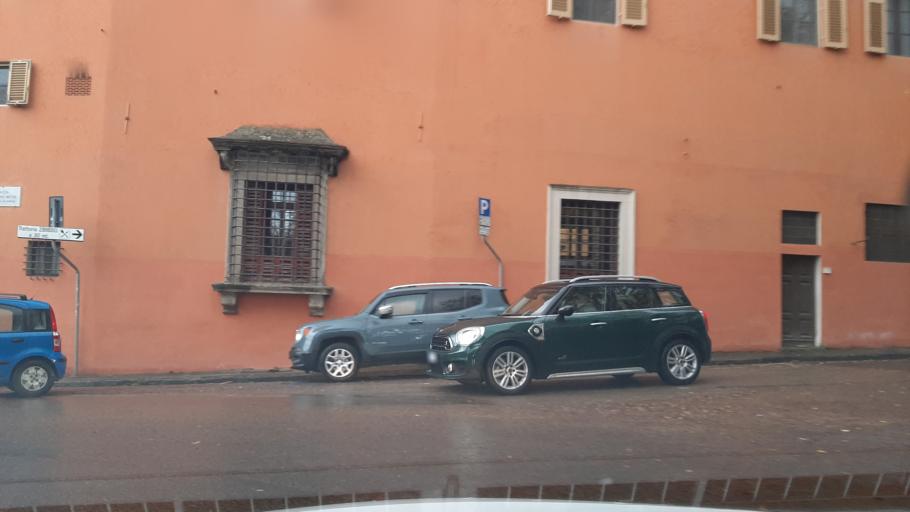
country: IT
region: Tuscany
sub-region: Province of Florence
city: Florence
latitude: 43.8130
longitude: 11.2510
